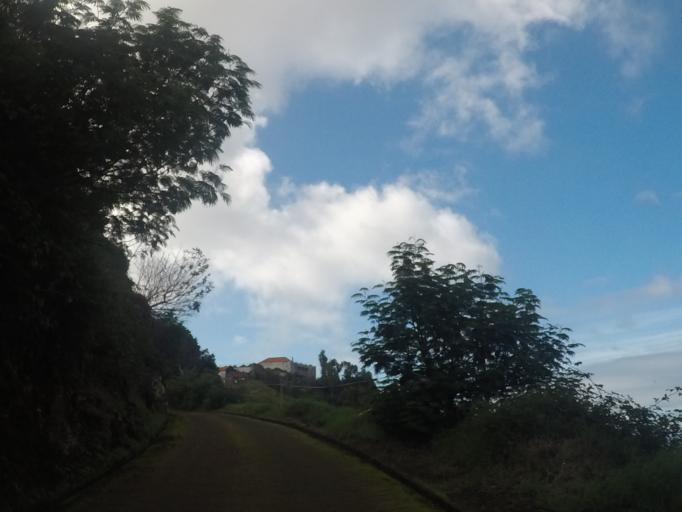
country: PT
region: Madeira
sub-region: Calheta
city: Faja da Ovelha
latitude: 32.8141
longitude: -17.2439
